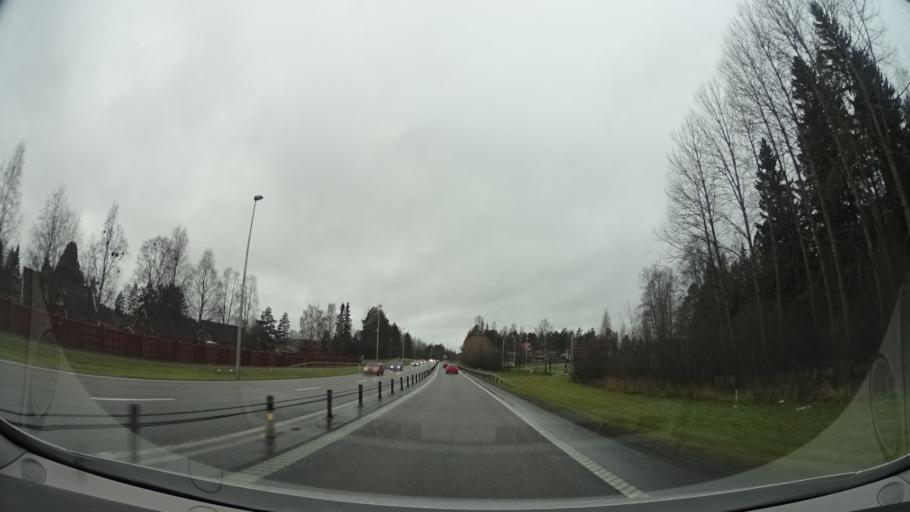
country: SE
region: Vaesterbotten
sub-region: Skelleftea Kommun
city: Skelleftea
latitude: 64.7612
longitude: 20.9851
